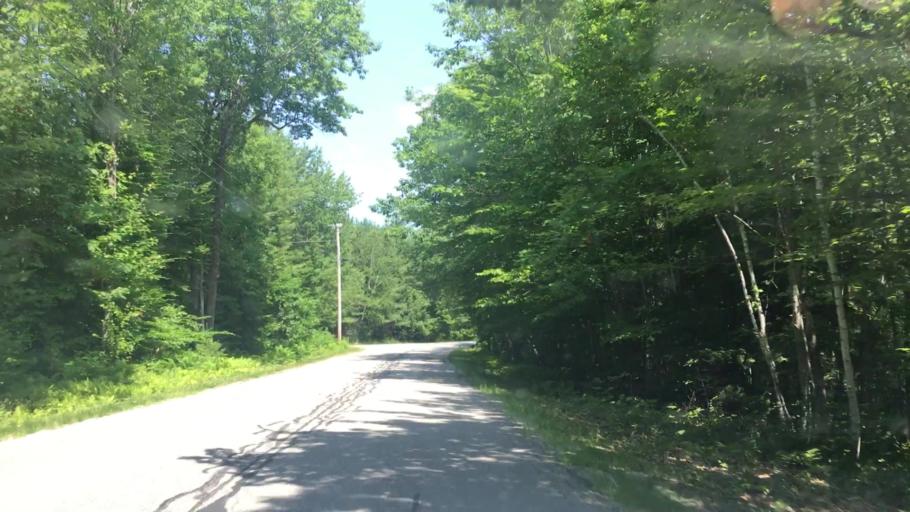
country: US
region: Maine
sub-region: Kennebec County
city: Wayne
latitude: 44.3181
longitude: -70.0584
